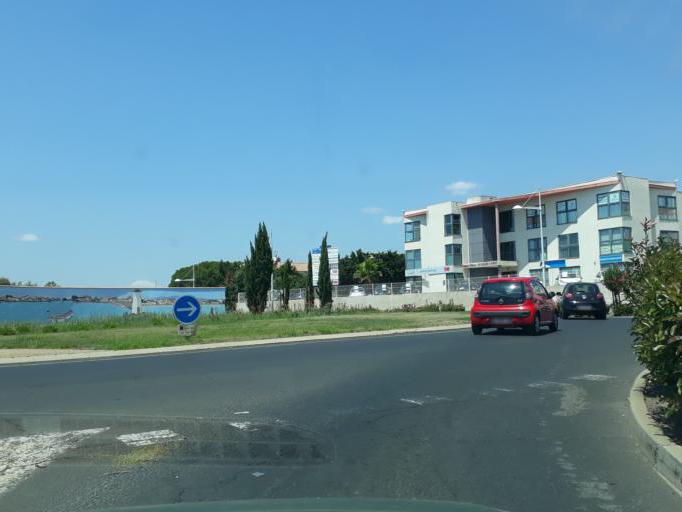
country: FR
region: Languedoc-Roussillon
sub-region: Departement de l'Herault
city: Agde
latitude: 43.3001
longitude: 3.4724
